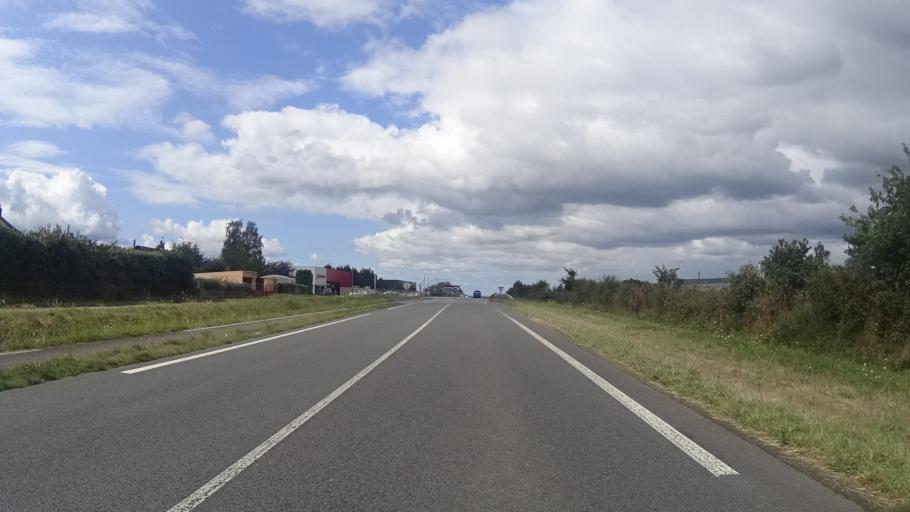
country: FR
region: Pays de la Loire
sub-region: Departement de la Loire-Atlantique
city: Savenay
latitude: 47.3652
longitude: -1.9460
